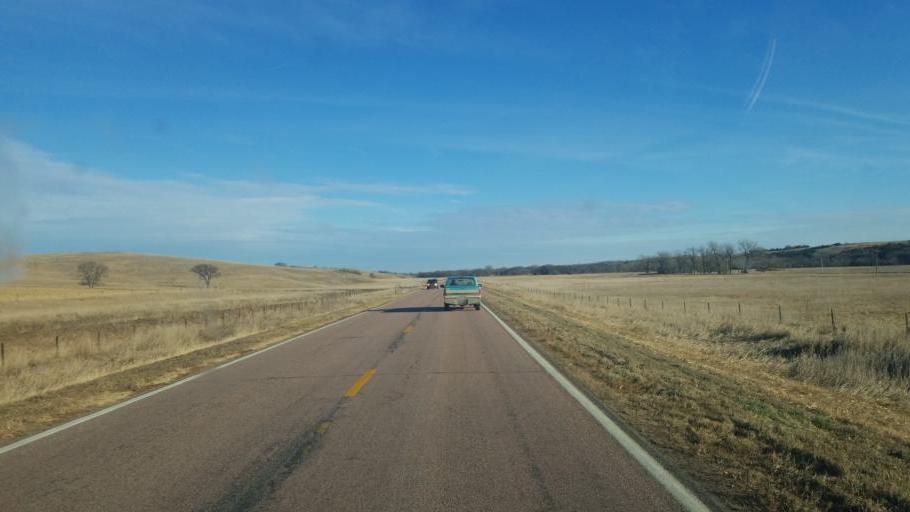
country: US
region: South Dakota
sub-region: Charles Mix County
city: Wagner
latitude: 42.8300
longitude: -98.4455
